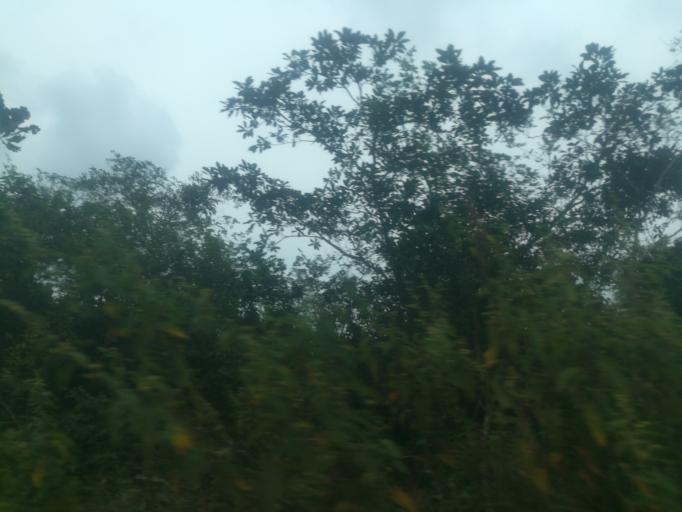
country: NG
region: Ogun
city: Ayetoro
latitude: 7.0981
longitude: 3.1235
